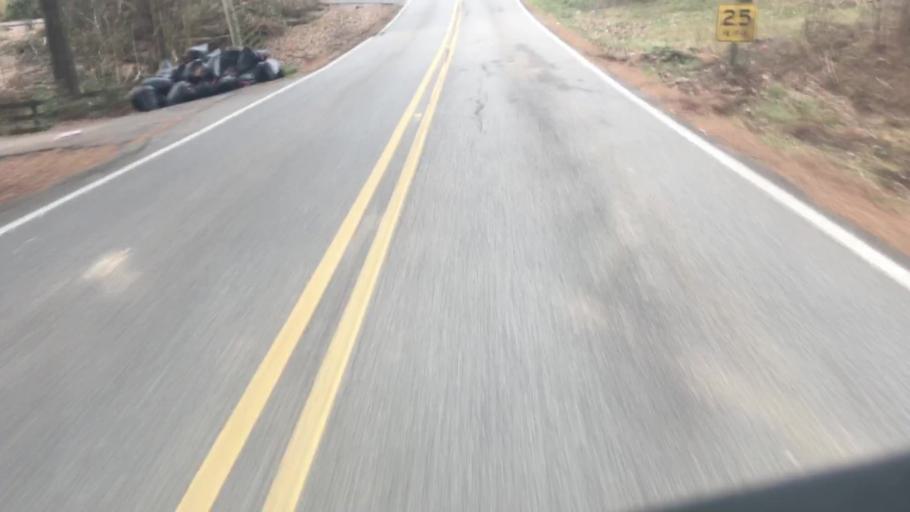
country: US
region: Alabama
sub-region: Jefferson County
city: Vestavia Hills
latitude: 33.4134
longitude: -86.7643
